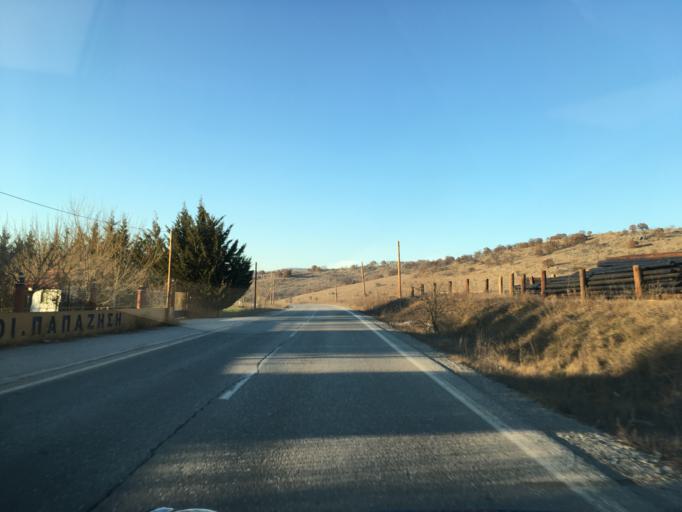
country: GR
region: West Macedonia
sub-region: Nomos Kozanis
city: Kozani
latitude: 40.3044
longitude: 21.7361
